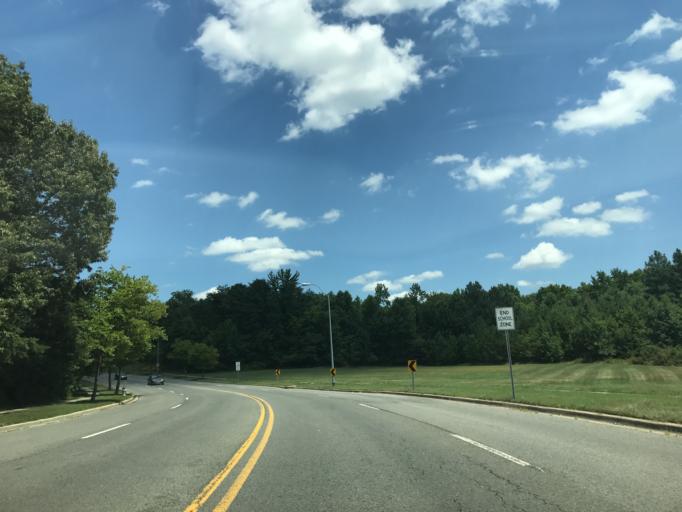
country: US
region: Maryland
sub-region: Prince George's County
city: South Laurel
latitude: 39.0524
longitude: -76.8441
